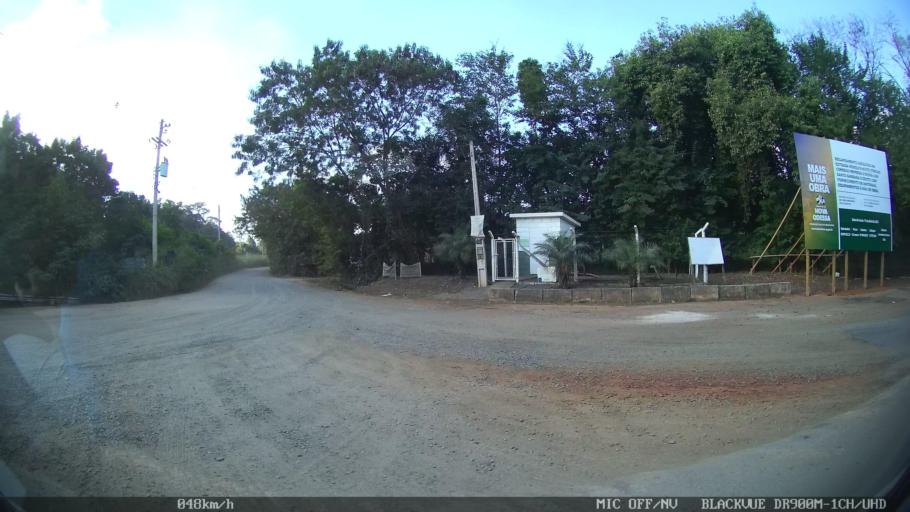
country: BR
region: Sao Paulo
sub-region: Nova Odessa
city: Nova Odessa
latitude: -22.7948
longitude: -47.3362
